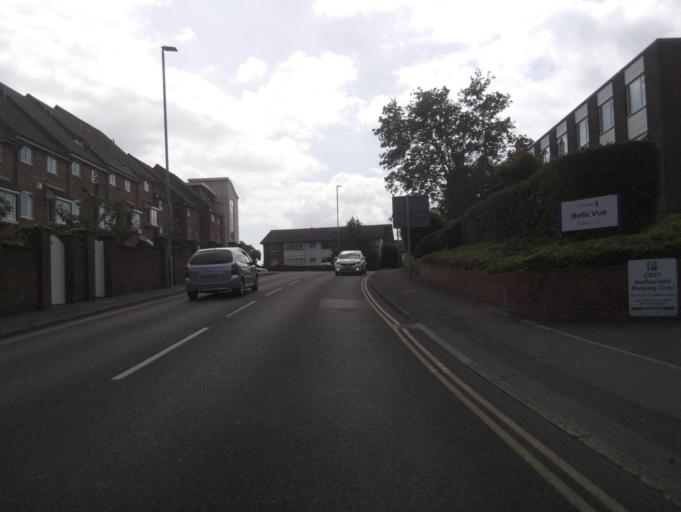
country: GB
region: England
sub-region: Poole
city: Poole
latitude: 50.7194
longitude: -1.9733
